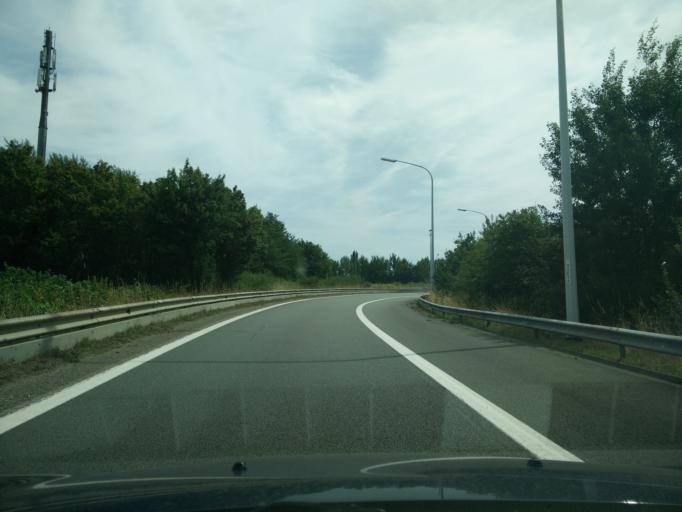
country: BE
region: Flanders
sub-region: Provincie Oost-Vlaanderen
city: Melle
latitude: 51.0107
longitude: 3.7869
